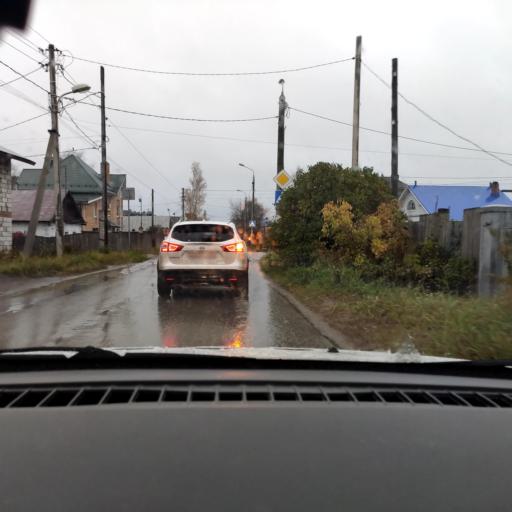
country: RU
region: Perm
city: Kondratovo
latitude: 58.0455
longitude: 56.1196
